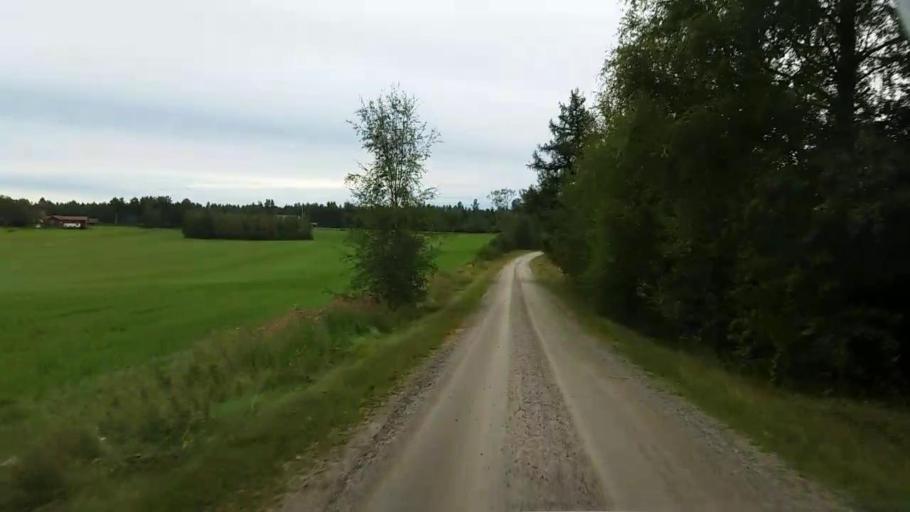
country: SE
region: Gaevleborg
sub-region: Ljusdals Kommun
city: Farila
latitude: 61.8104
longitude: 15.8636
